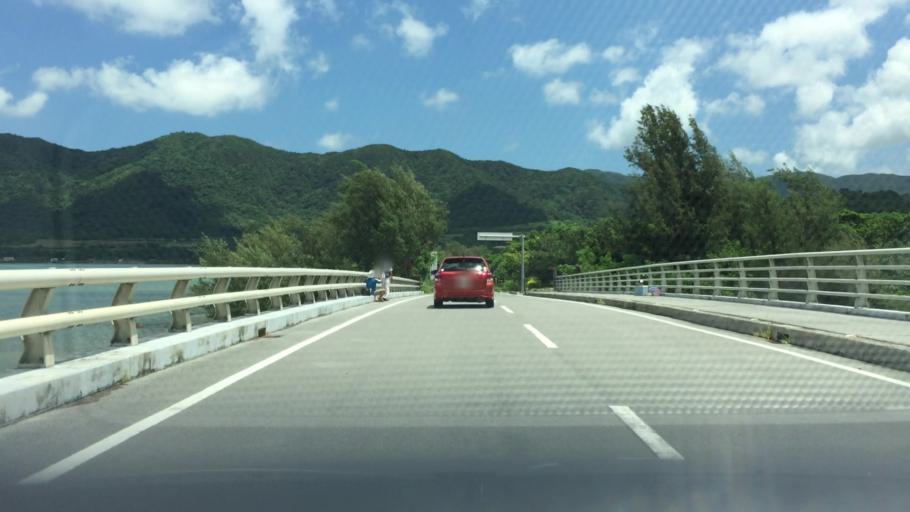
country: JP
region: Okinawa
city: Ishigaki
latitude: 24.4023
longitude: 124.1410
